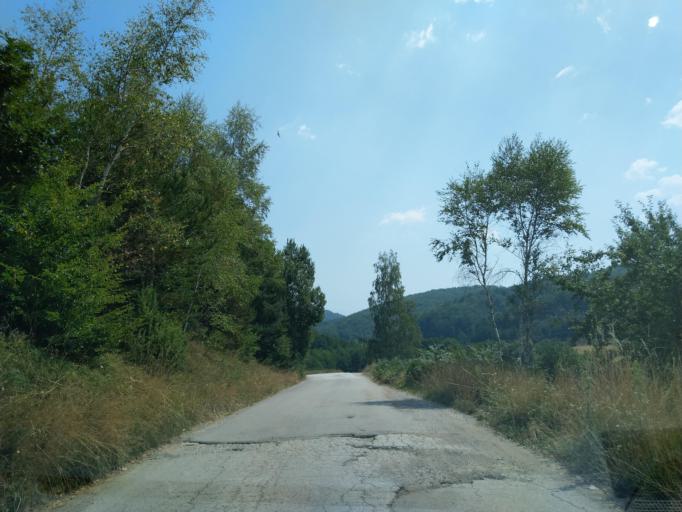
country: RS
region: Central Serbia
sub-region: Zlatiborski Okrug
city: Prijepolje
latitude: 43.3330
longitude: 19.5617
